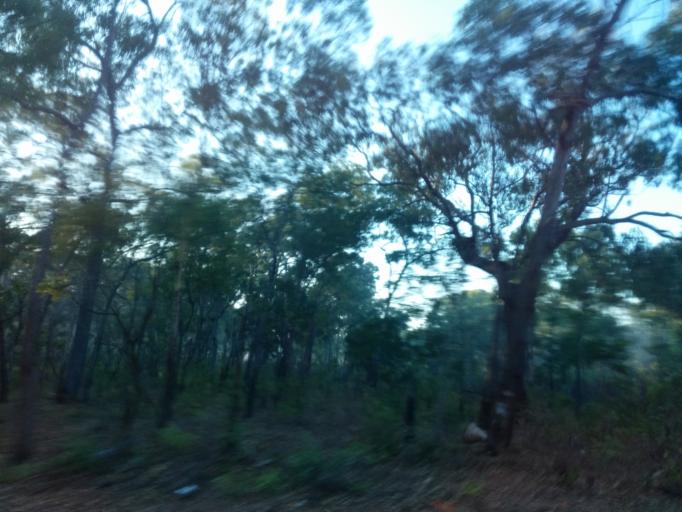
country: AU
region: Northern Territory
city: Alyangula
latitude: -13.8658
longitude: 136.8033
